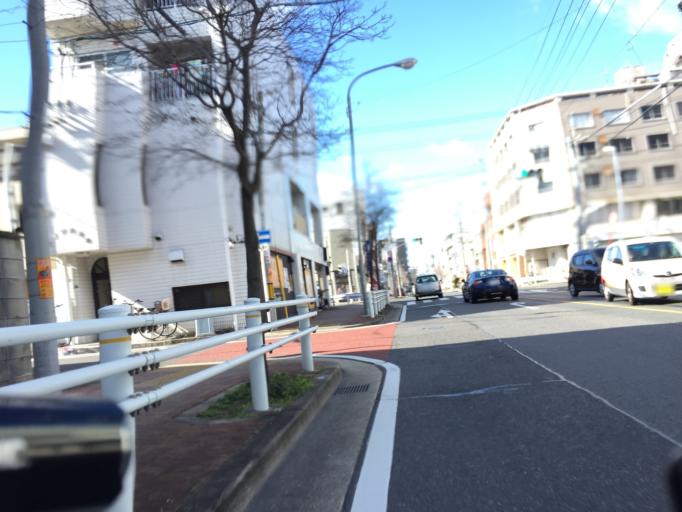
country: JP
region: Aichi
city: Nagoya-shi
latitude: 35.1625
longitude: 136.9311
